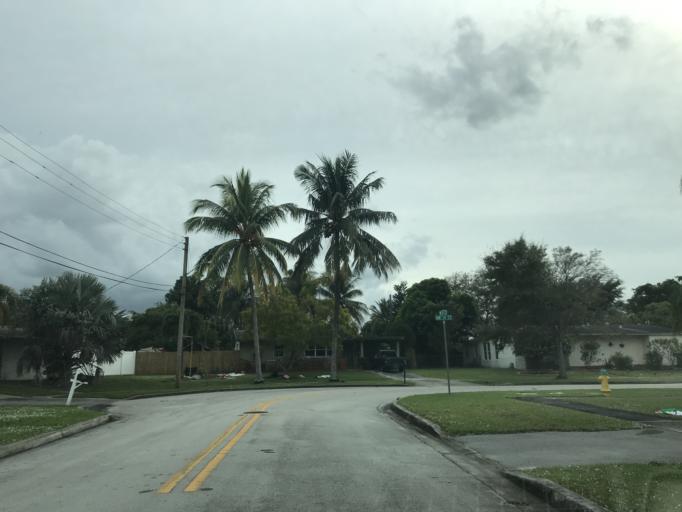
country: US
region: Florida
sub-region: Broward County
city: Margate
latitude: 26.2527
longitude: -80.2047
